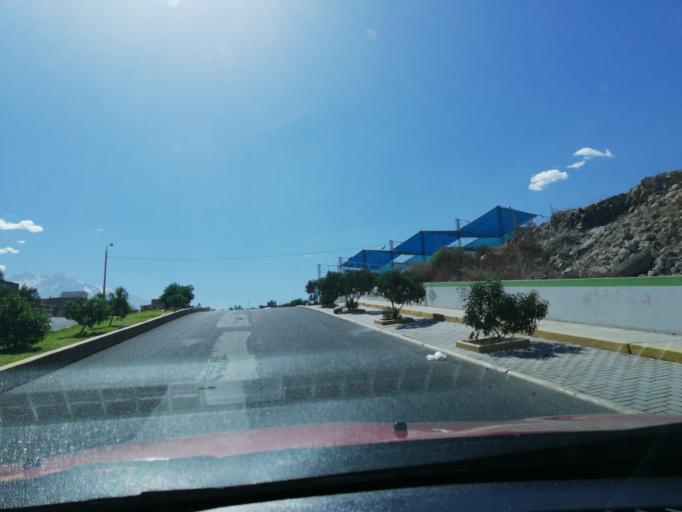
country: PE
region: Arequipa
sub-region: Provincia de Arequipa
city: Arequipa
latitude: -16.3677
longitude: -71.5247
